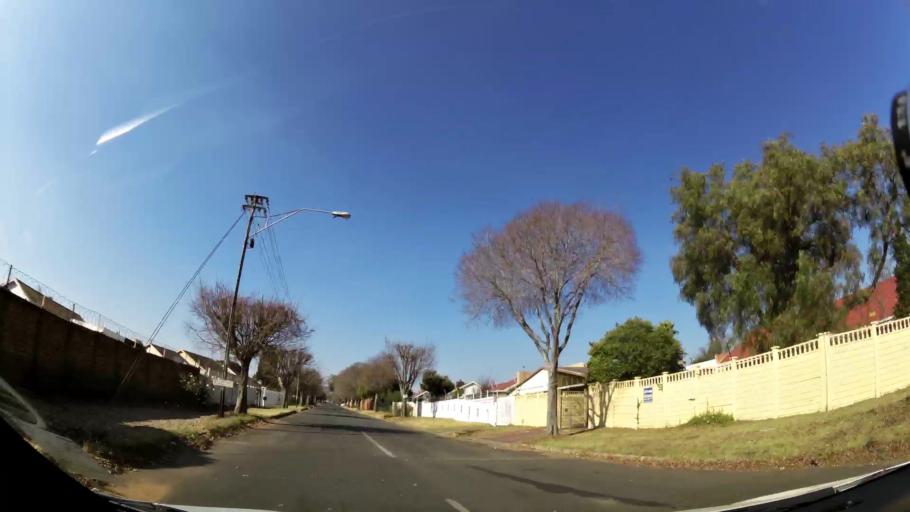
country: ZA
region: Gauteng
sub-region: City of Johannesburg Metropolitan Municipality
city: Johannesburg
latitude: -26.2565
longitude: 27.9973
